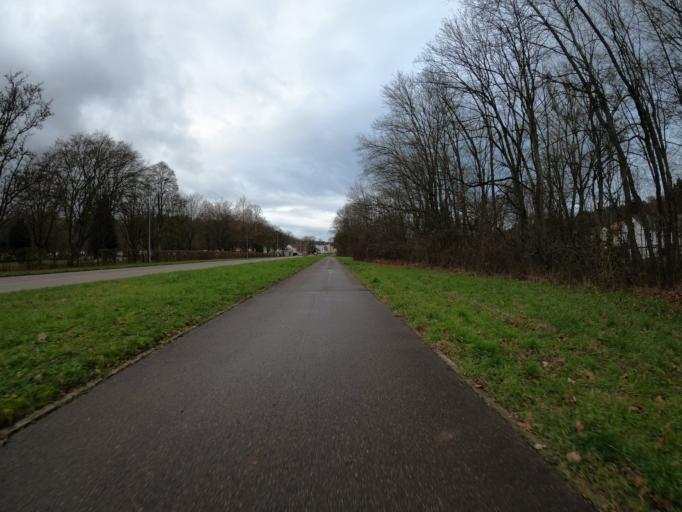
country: DE
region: Baden-Wuerttemberg
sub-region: Regierungsbezirk Stuttgart
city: Schwabisch Gmund
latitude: 48.7886
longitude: 9.8175
